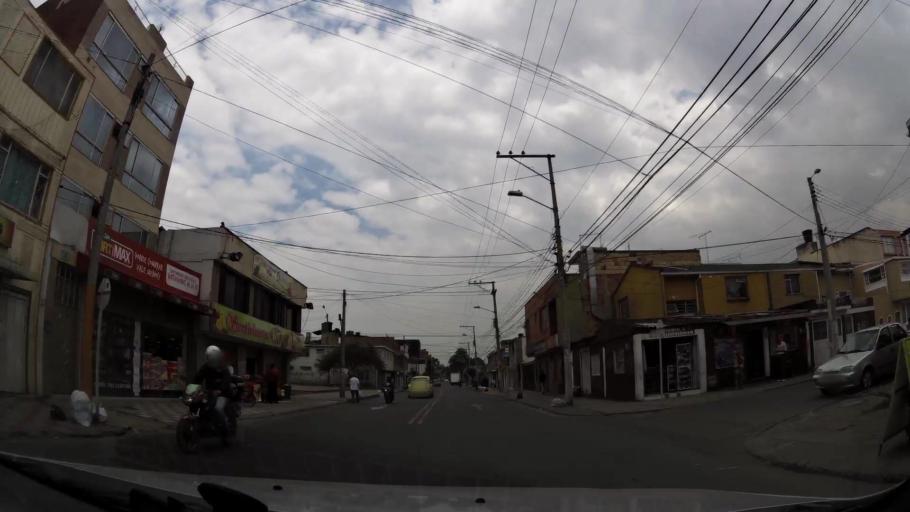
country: CO
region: Bogota D.C.
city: Bogota
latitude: 4.5950
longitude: -74.1089
